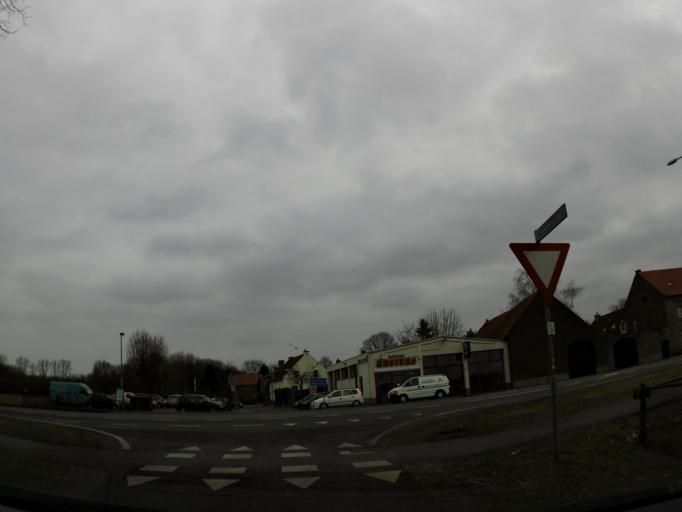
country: BE
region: Flanders
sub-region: Provincie Limburg
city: Maaseik
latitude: 51.0840
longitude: 5.8073
